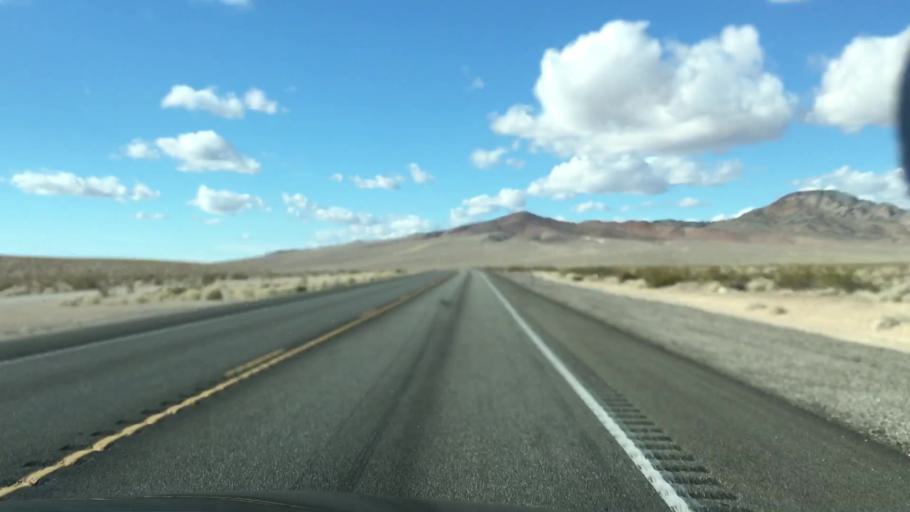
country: US
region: Nevada
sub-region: Nye County
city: Beatty
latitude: 36.6288
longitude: -116.3140
